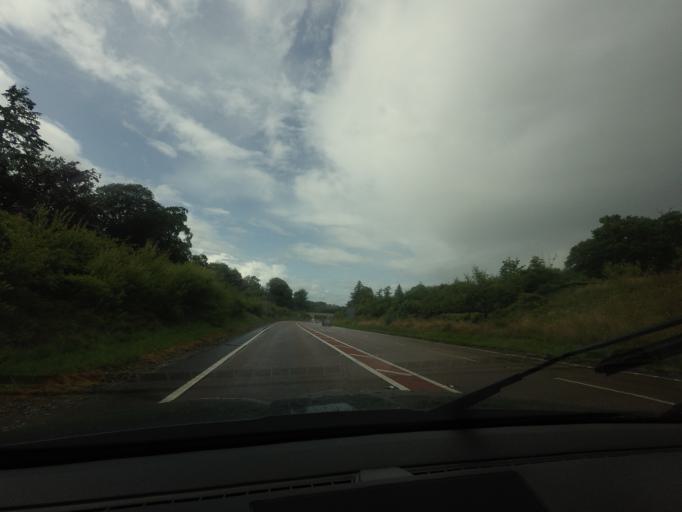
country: GB
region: Scotland
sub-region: Moray
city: Fochabers
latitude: 57.6159
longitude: -3.0976
